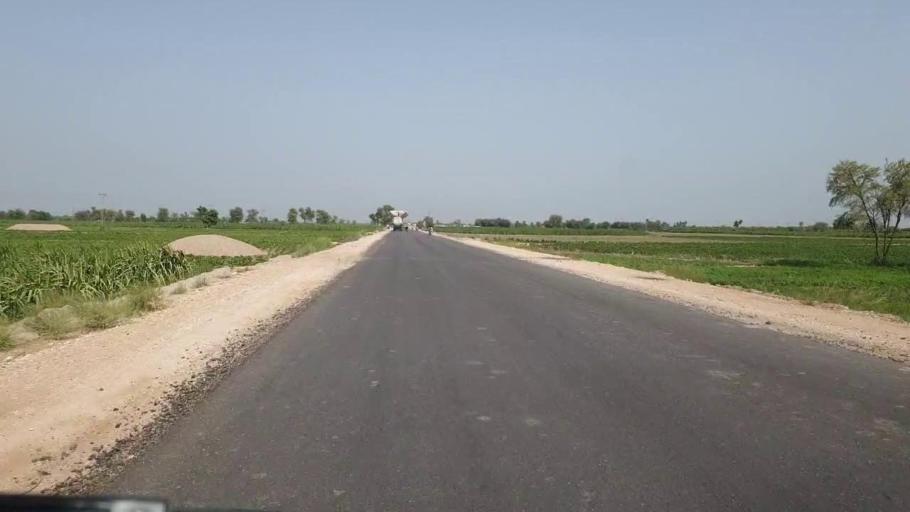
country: PK
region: Sindh
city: Sakrand
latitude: 26.2694
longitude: 68.1648
